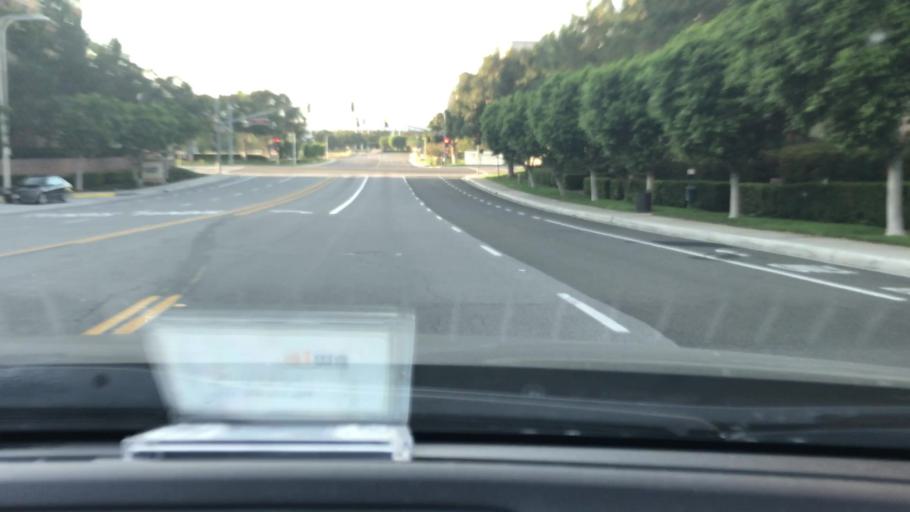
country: US
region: California
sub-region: Orange County
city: Laguna Woods
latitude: 33.6542
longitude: -117.7525
